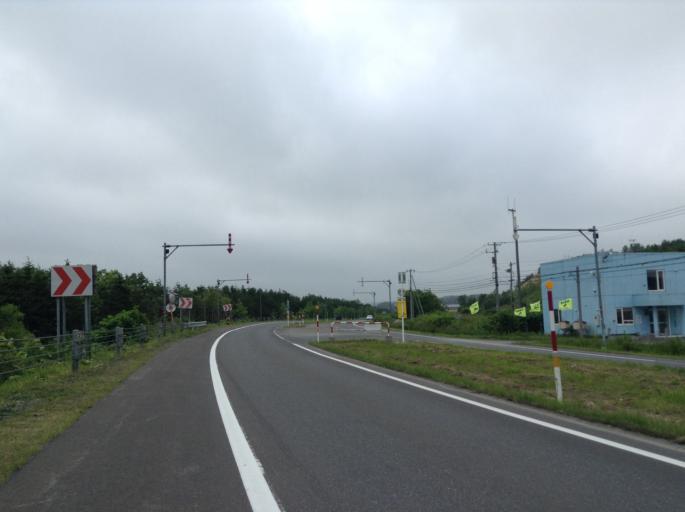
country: JP
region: Hokkaido
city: Wakkanai
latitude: 45.3688
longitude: 141.7270
